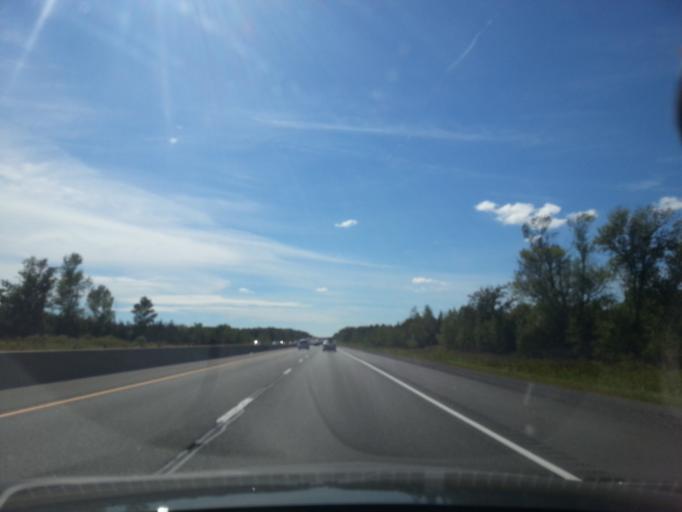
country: CA
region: Ontario
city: Belleville
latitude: 44.2157
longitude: -77.3170
